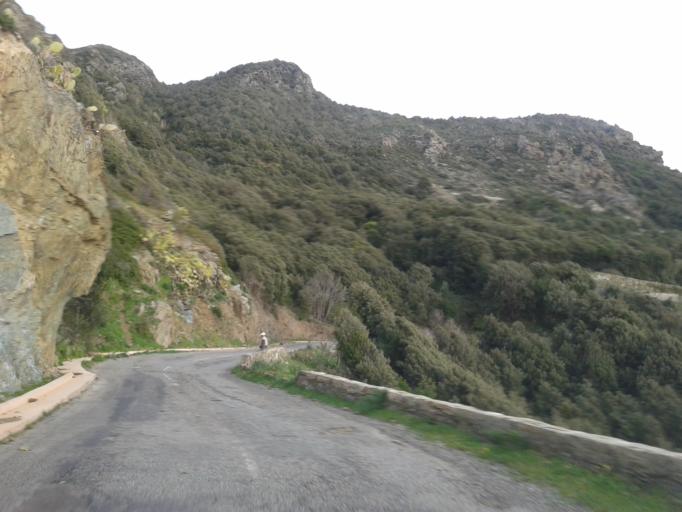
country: FR
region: Corsica
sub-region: Departement de la Haute-Corse
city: Brando
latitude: 42.8907
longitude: 9.3330
